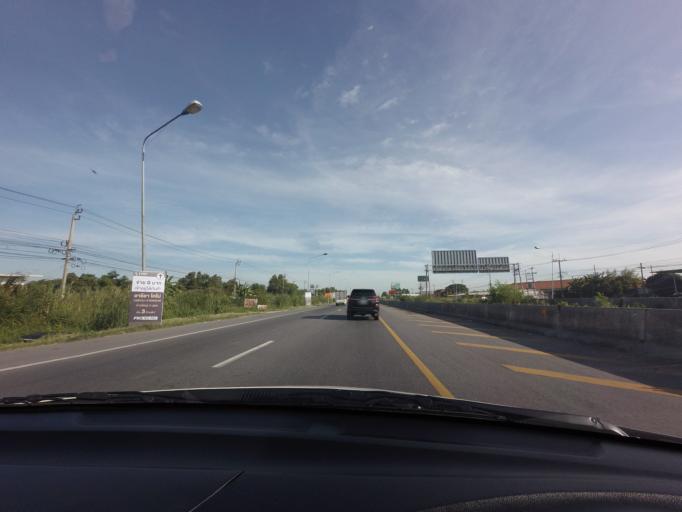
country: TH
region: Nonthaburi
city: Bang Bua Thong
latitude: 13.9468
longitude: 100.4131
